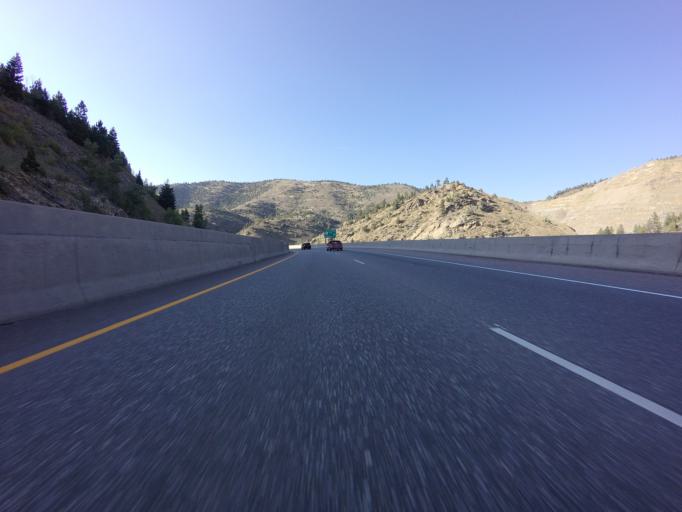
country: US
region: Colorado
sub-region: Clear Creek County
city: Idaho Springs
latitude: 39.7422
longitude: -105.4331
